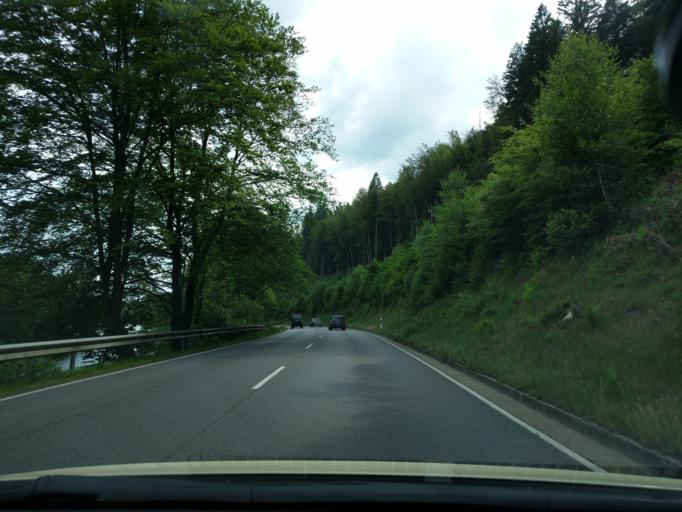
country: DE
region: Rheinland-Pfalz
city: Schopp
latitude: 49.3743
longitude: 7.6994
